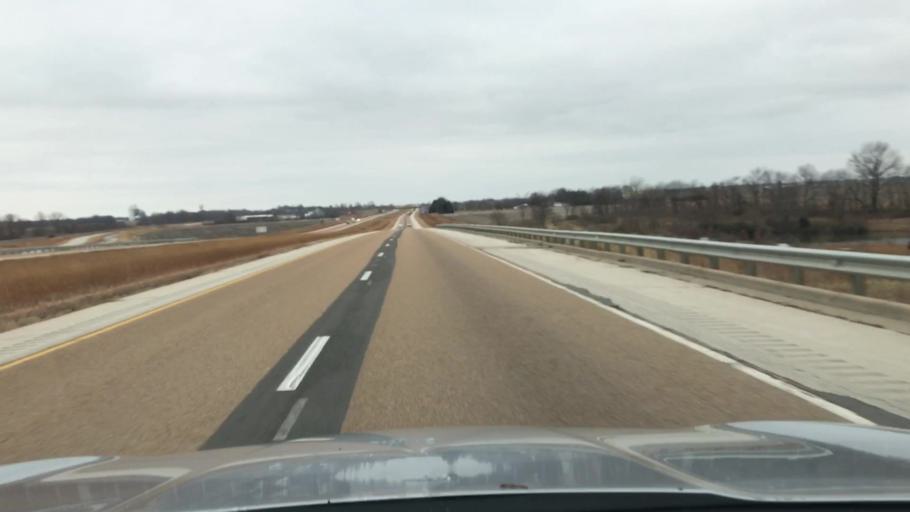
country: US
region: Illinois
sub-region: Montgomery County
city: Litchfield
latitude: 39.2147
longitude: -89.6524
